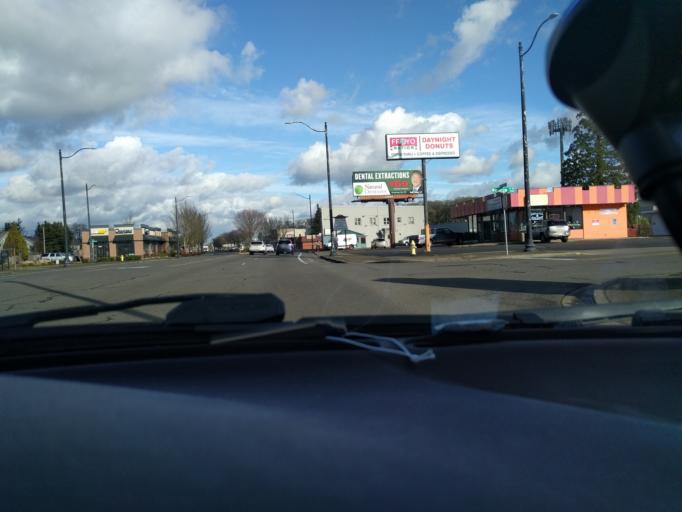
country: US
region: Oregon
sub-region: Marion County
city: Salem
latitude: 44.9579
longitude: -123.0179
